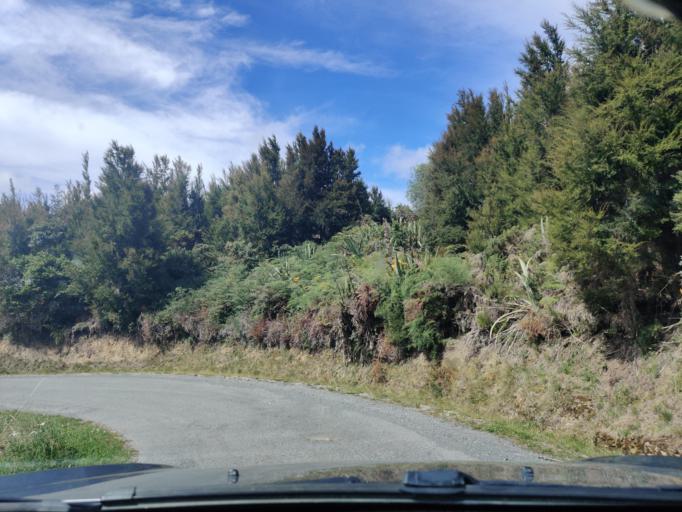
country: NZ
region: Tasman
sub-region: Tasman District
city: Wakefield
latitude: -41.6284
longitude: 172.7197
